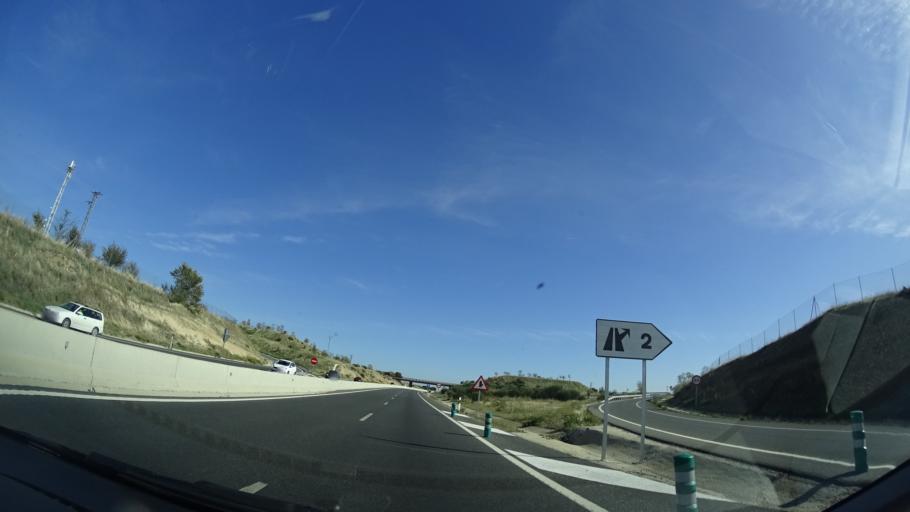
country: ES
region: Madrid
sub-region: Provincia de Madrid
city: Villanueva del Pardillo
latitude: 40.4827
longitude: -3.9260
